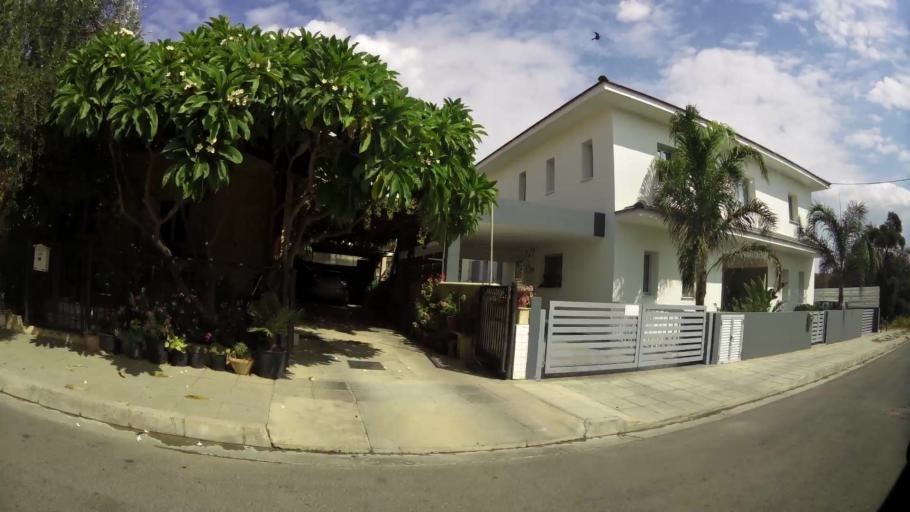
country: CY
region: Lefkosia
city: Tseri
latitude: 35.0701
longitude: 33.3307
